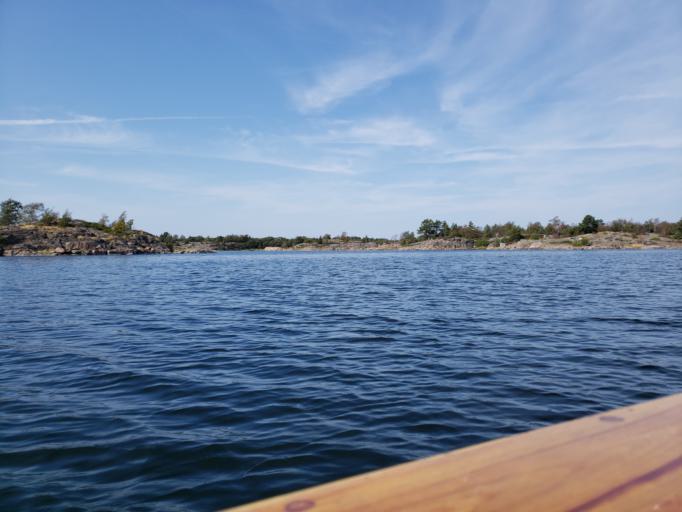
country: FI
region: Varsinais-Suomi
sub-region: Aboland-Turunmaa
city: Dragsfjaerd
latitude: 59.8492
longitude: 22.2104
